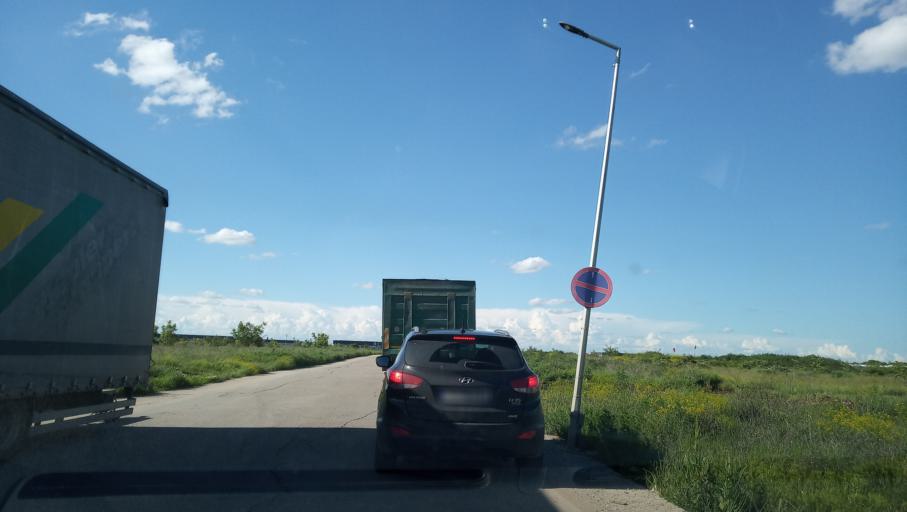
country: RO
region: Ilfov
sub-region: Comuna Chiajna
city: Chiajna
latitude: 44.4472
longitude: 25.9580
